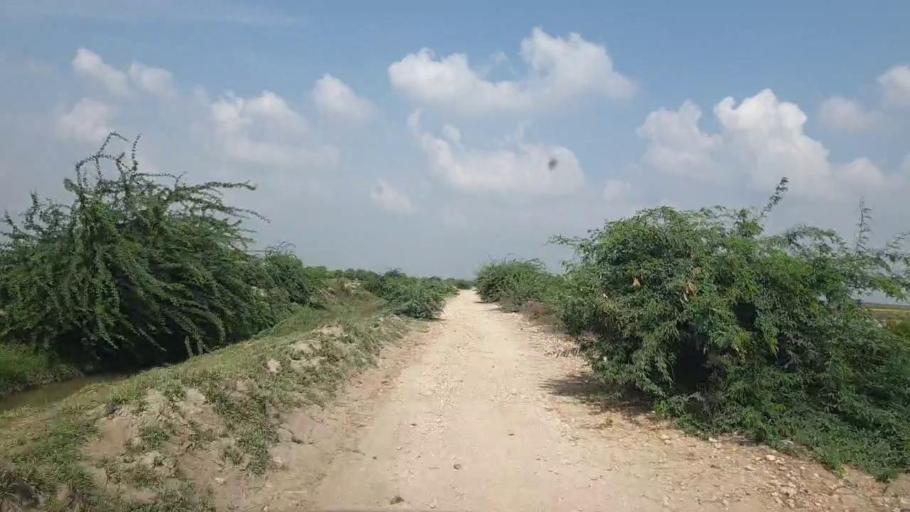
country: PK
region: Sindh
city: Badin
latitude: 24.4958
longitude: 68.6558
